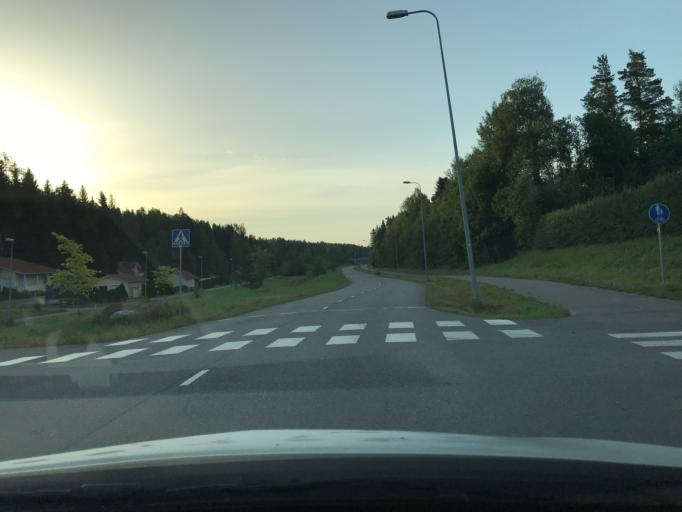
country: FI
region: Uusimaa
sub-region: Helsinki
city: Vihti
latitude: 60.4041
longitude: 24.4832
